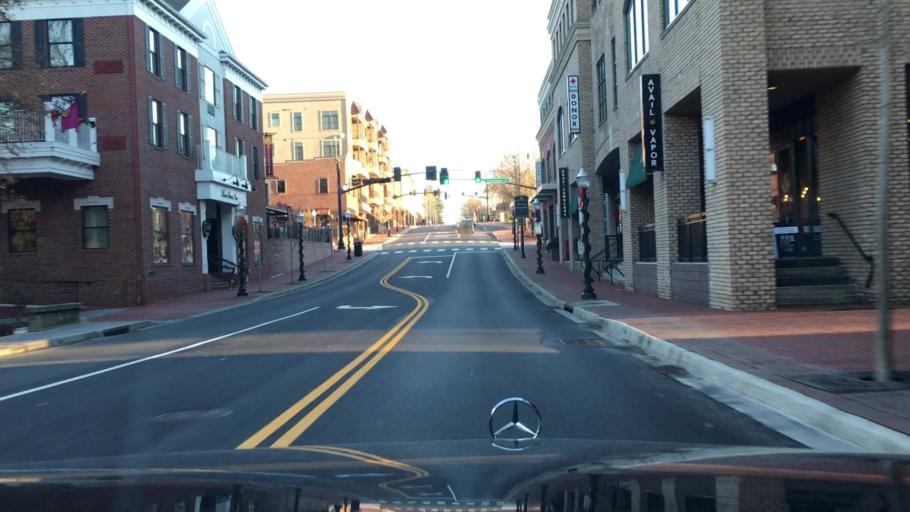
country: US
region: Virginia
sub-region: Montgomery County
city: Blacksburg
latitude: 37.2285
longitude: -80.4131
